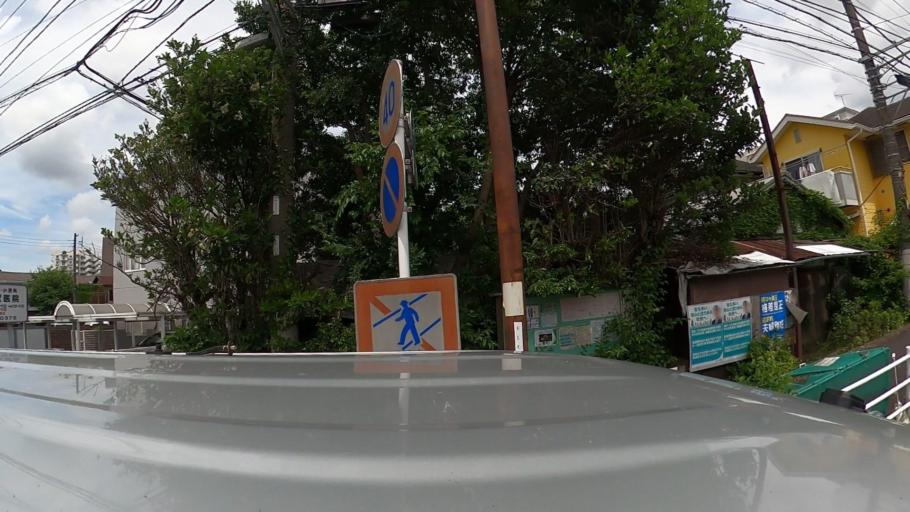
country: JP
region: Kanagawa
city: Fujisawa
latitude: 35.4069
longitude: 139.5380
